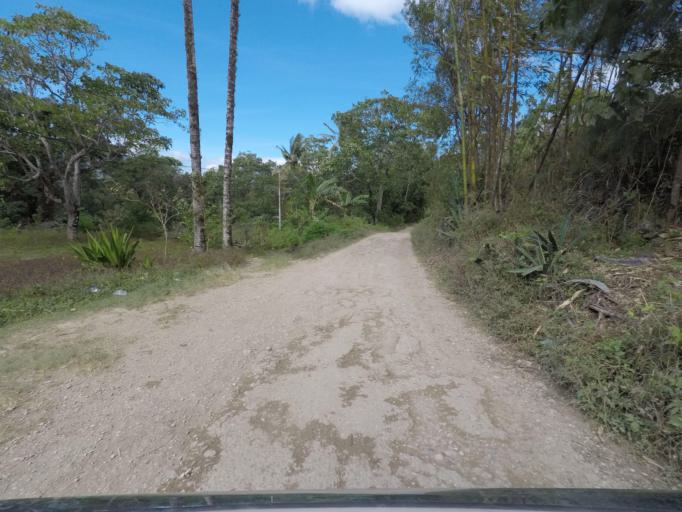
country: TL
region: Baucau
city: Venilale
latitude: -8.6420
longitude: 126.3809
